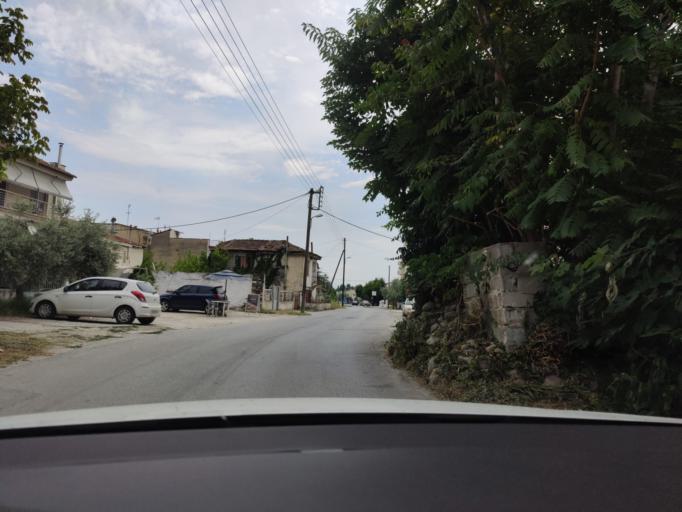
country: GR
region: Central Macedonia
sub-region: Nomos Serron
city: Serres
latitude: 41.0831
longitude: 23.5339
